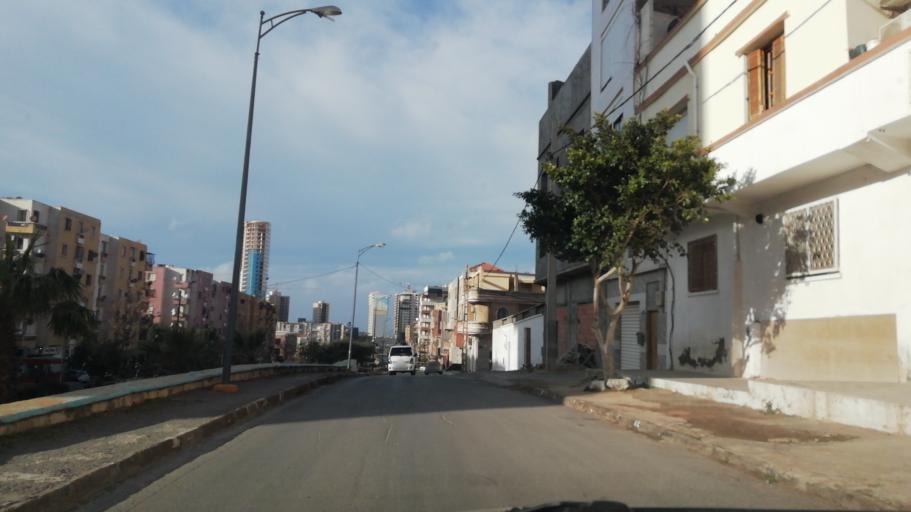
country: DZ
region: Oran
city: Bir el Djir
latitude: 35.7235
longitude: -0.5840
